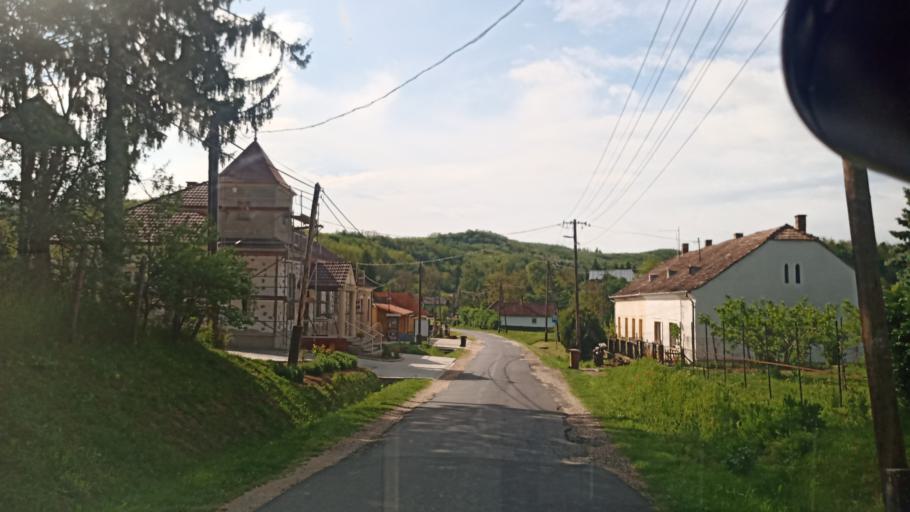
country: HU
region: Zala
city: Pacsa
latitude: 46.6727
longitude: 17.0774
